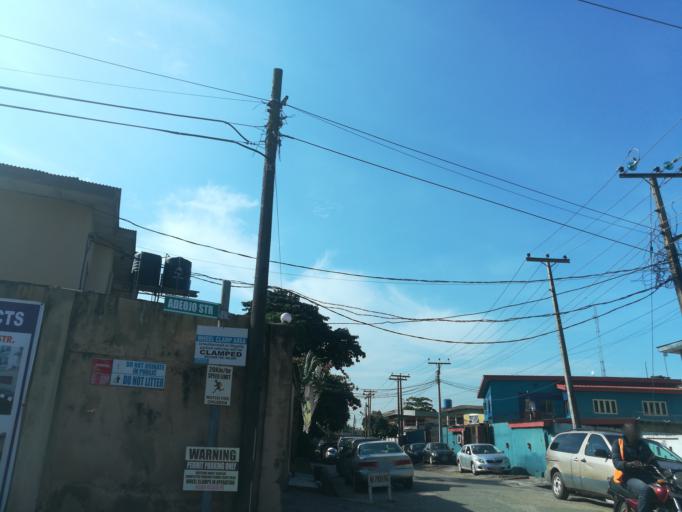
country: NG
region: Lagos
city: Ikeja
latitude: 6.6046
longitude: 3.3402
